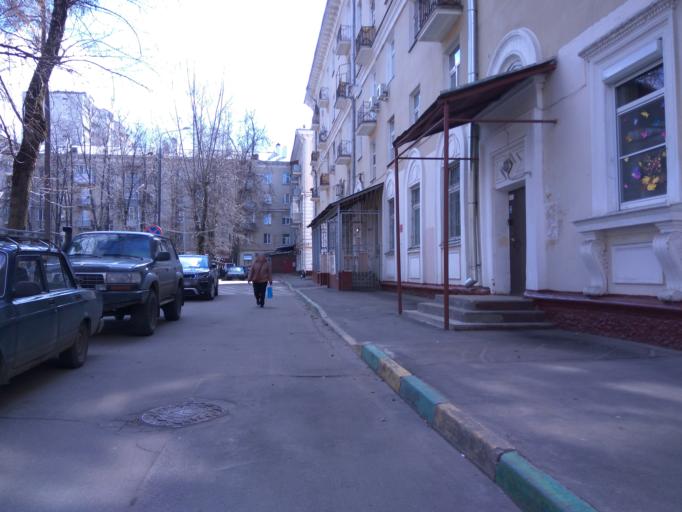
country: RU
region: Moskovskaya
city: Izmaylovo
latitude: 55.7945
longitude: 37.8130
